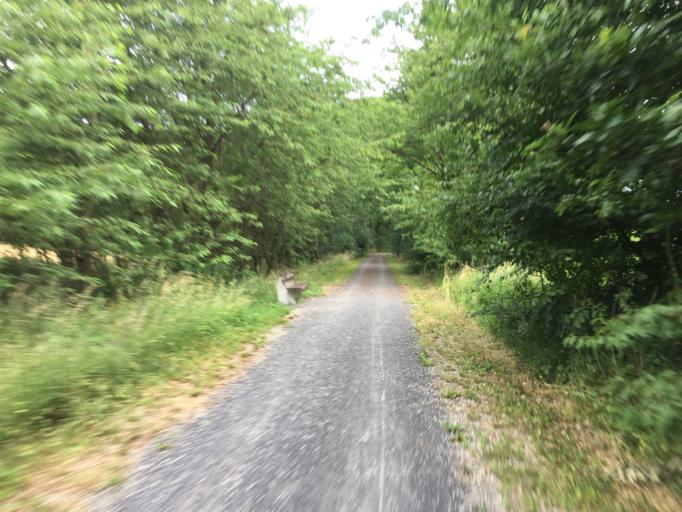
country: DE
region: Hesse
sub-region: Regierungsbezirk Kassel
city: Lohfelden
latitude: 51.2450
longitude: 9.5557
